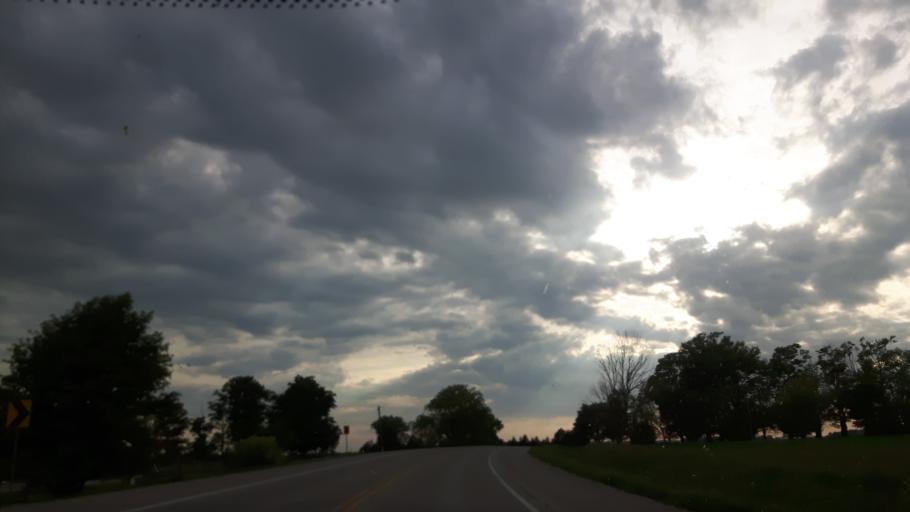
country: CA
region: Ontario
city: Bluewater
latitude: 43.5222
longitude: -81.5488
